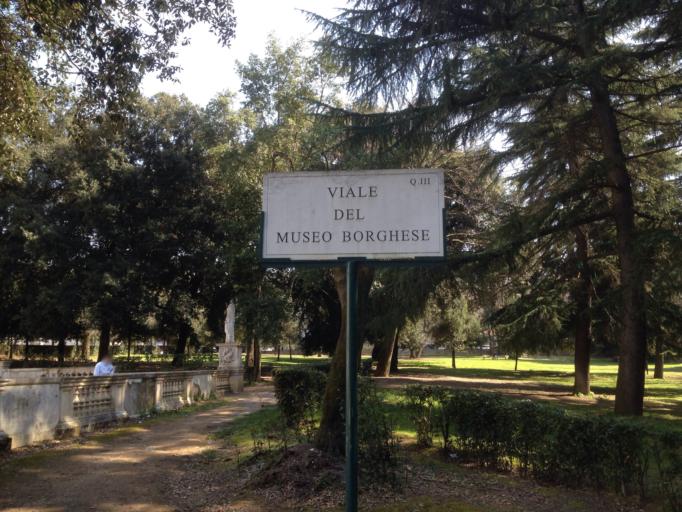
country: IT
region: Latium
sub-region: Citta metropolitana di Roma Capitale
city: Rome
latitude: 41.9137
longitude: 12.4917
